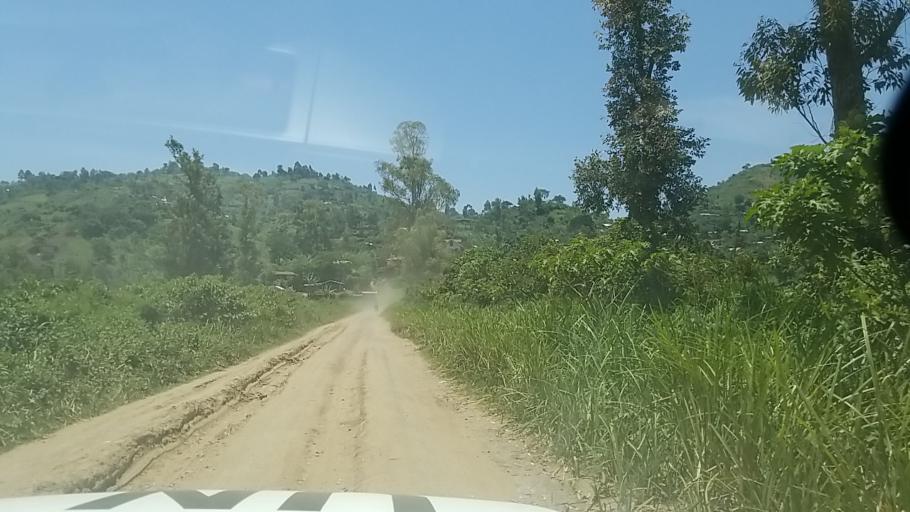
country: CD
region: Nord Kivu
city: Sake
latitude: -1.8060
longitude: 29.0128
